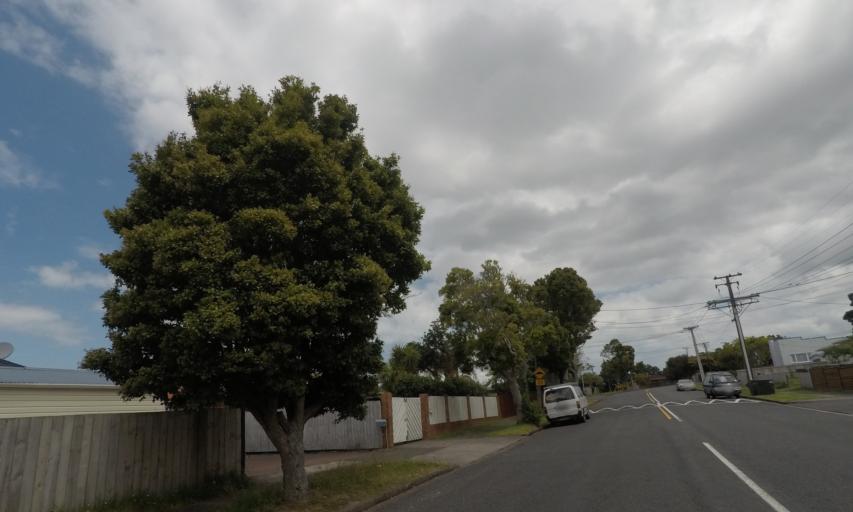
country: NZ
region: Auckland
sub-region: Auckland
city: Waitakere
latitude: -36.9053
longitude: 174.6693
